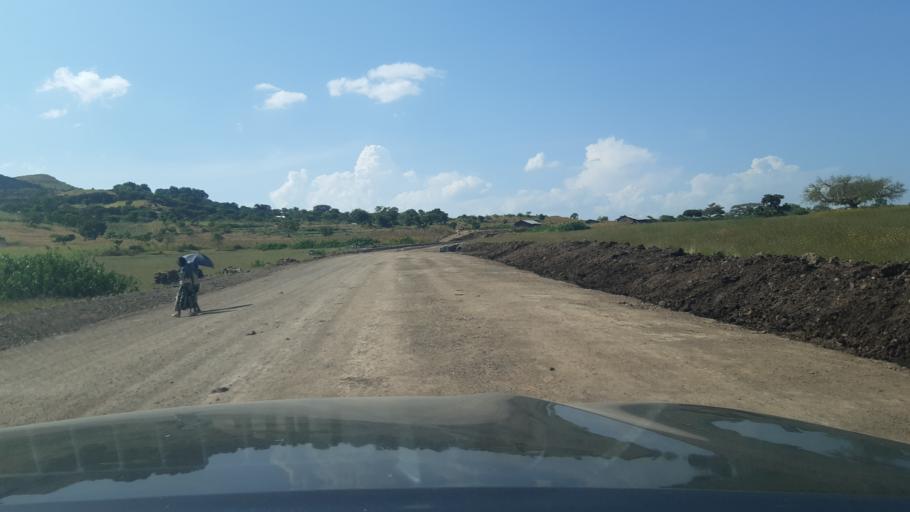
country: ET
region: Amhara
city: Dabat
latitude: 13.1589
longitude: 37.6090
